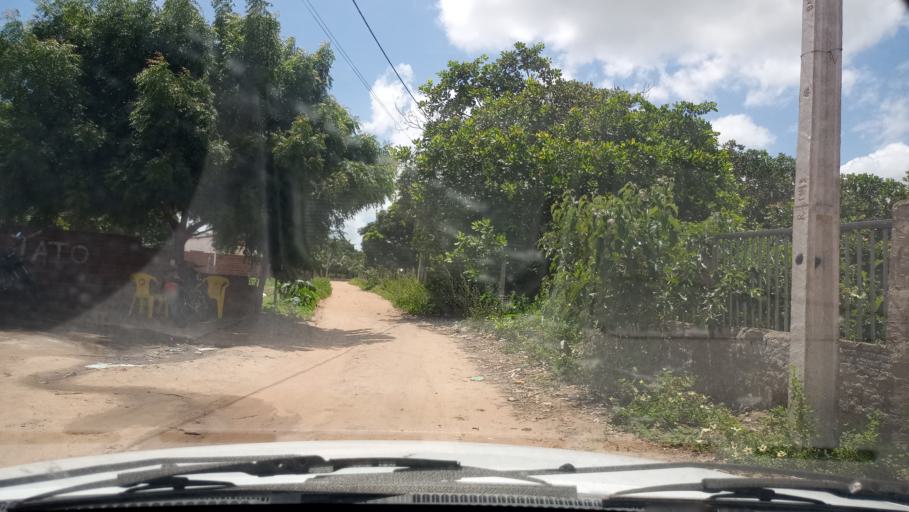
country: BR
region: Rio Grande do Norte
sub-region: Brejinho
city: Brejinho
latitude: -6.2641
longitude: -35.3738
